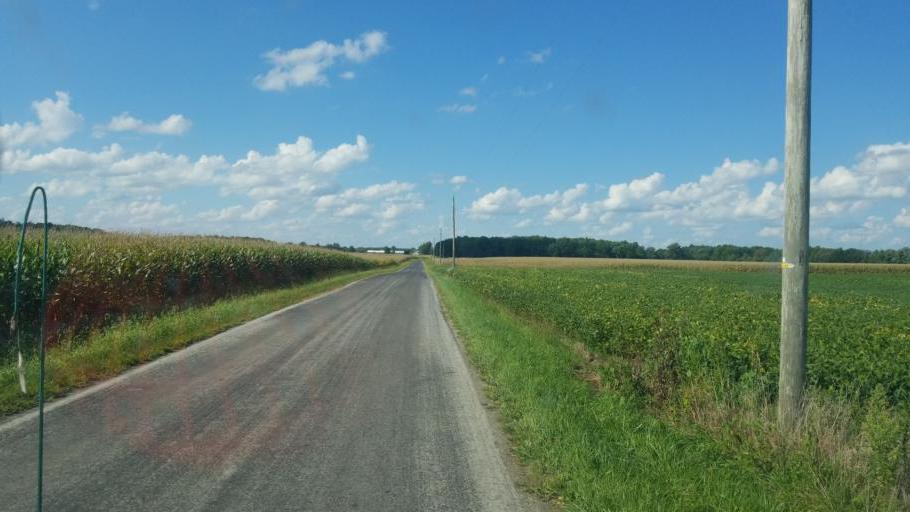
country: US
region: Ohio
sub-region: Union County
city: Richwood
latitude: 40.5748
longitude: -83.4069
